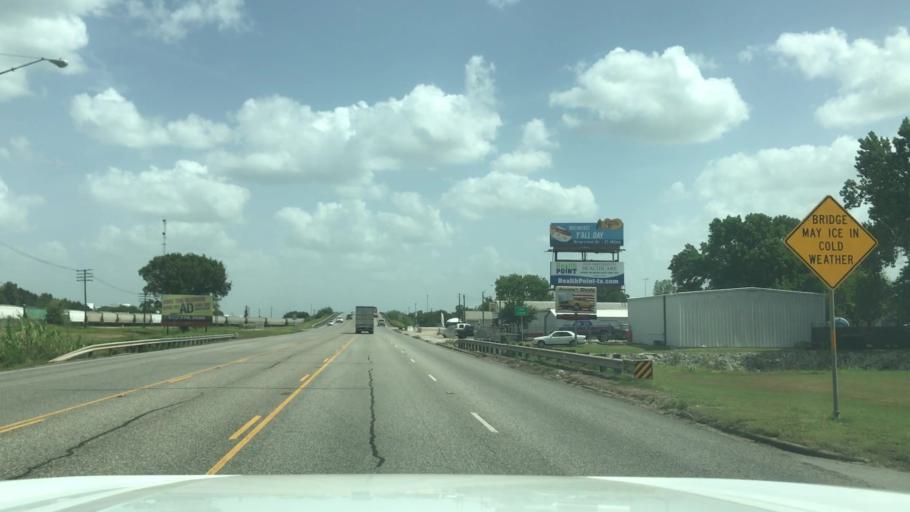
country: US
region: Texas
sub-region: Robertson County
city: Hearne
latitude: 30.8717
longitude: -96.5879
